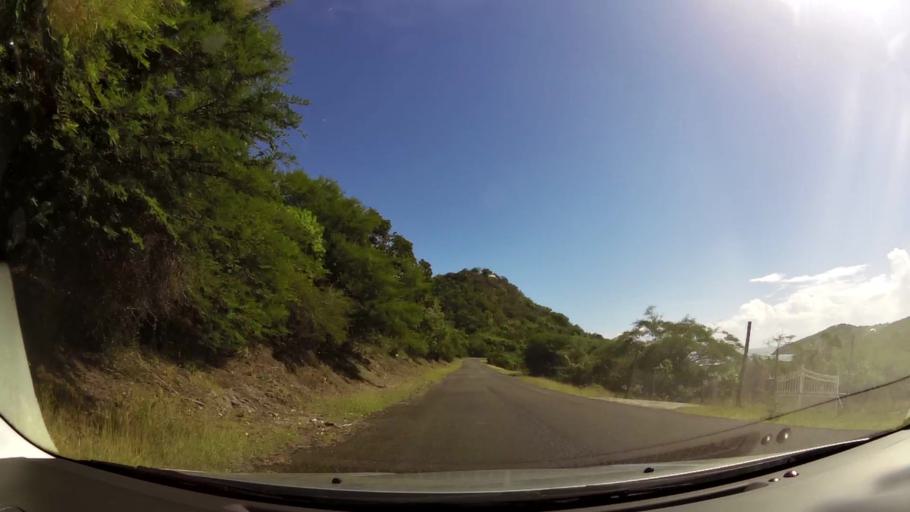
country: AG
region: Saint Paul
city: Falmouth
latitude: 17.0220
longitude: -61.7435
